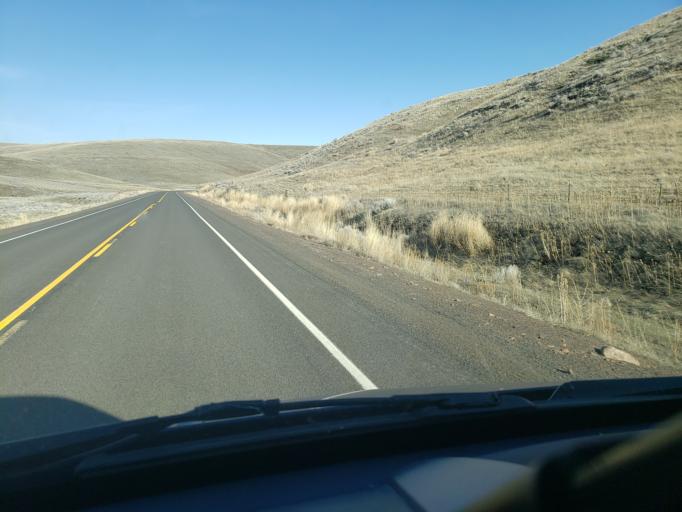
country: US
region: Oregon
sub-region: Umatilla County
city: Pilot Rock
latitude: 45.4665
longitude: -118.9193
